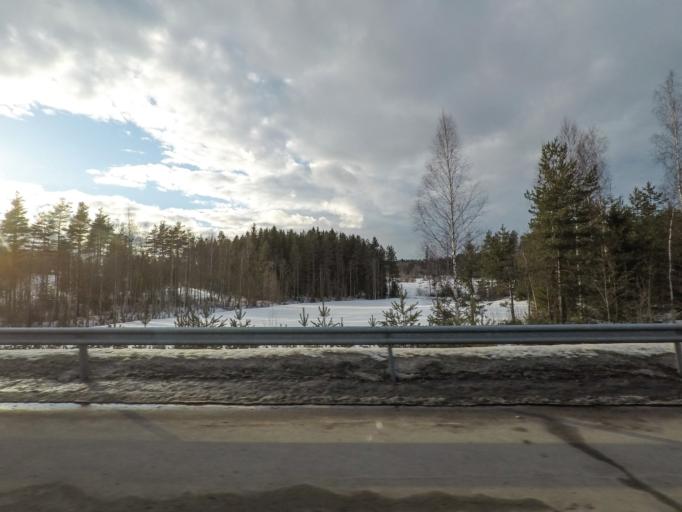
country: FI
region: Paijanne Tavastia
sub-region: Lahti
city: Nastola
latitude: 61.0712
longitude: 25.8817
